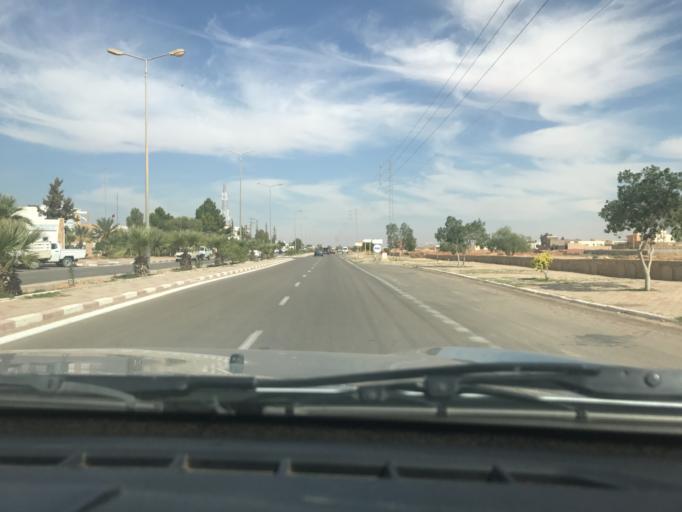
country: TN
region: Tataouine
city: Tataouine
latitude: 32.9928
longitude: 10.4625
